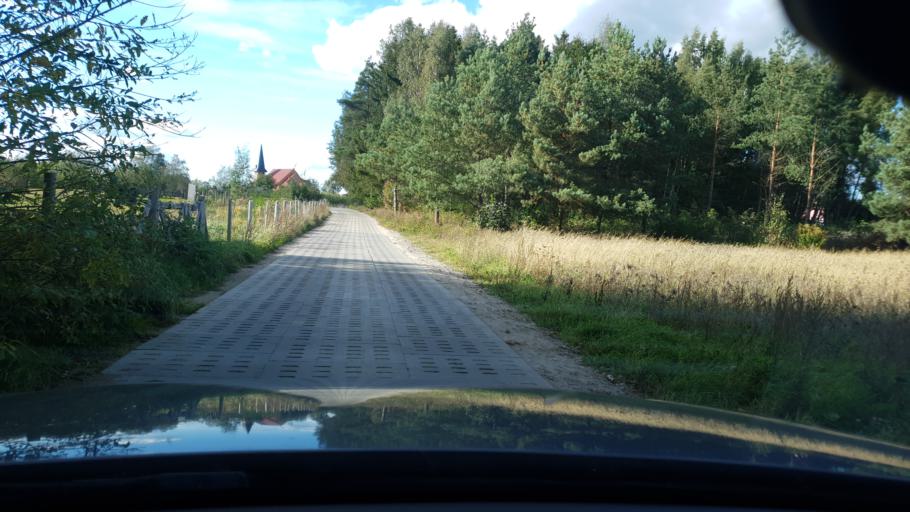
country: PL
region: Pomeranian Voivodeship
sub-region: Powiat kartuski
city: Chwaszczyno
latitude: 54.4834
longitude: 18.4247
